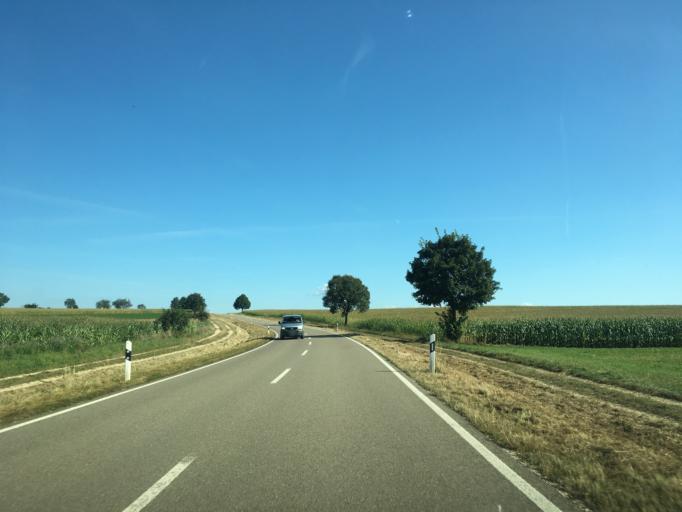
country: DE
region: Baden-Wuerttemberg
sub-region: Tuebingen Region
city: Rechtenstein
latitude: 48.2502
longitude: 9.5383
